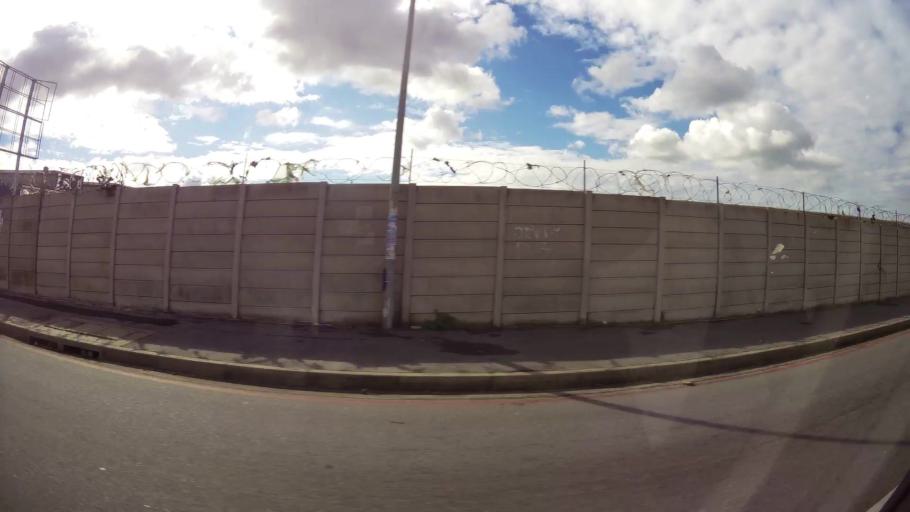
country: ZA
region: Eastern Cape
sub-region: Nelson Mandela Bay Metropolitan Municipality
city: Port Elizabeth
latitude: -33.9293
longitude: 25.5760
